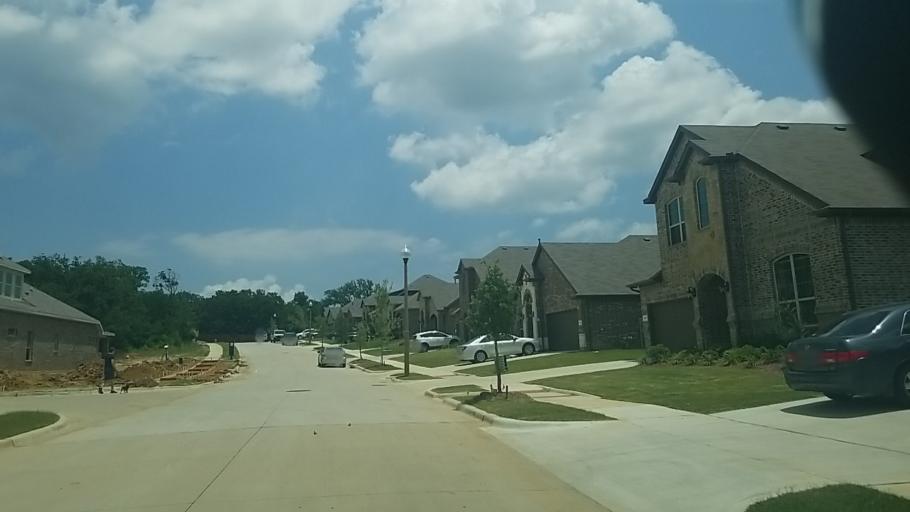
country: US
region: Texas
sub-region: Denton County
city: Denton
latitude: 33.1685
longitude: -97.1150
